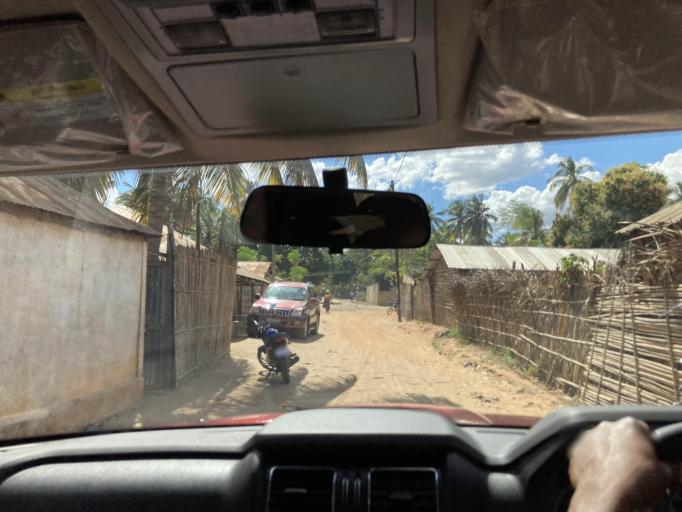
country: MZ
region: Cabo Delgado
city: Montepuez
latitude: -13.1346
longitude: 39.0055
